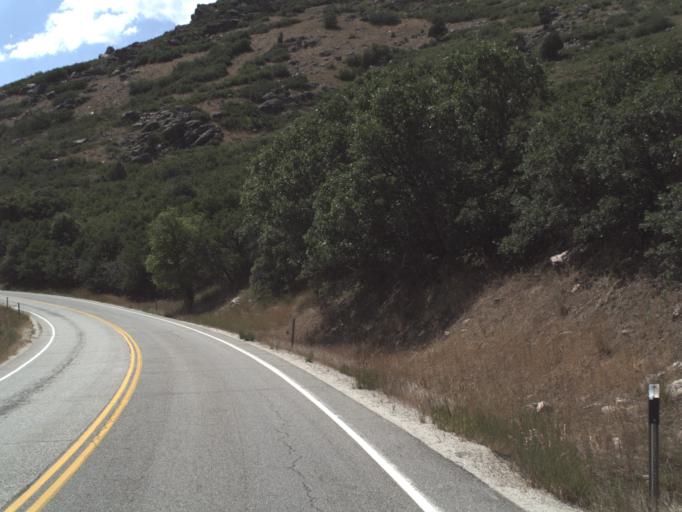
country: US
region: Utah
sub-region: Weber County
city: Wolf Creek
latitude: 41.2669
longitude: -111.6802
